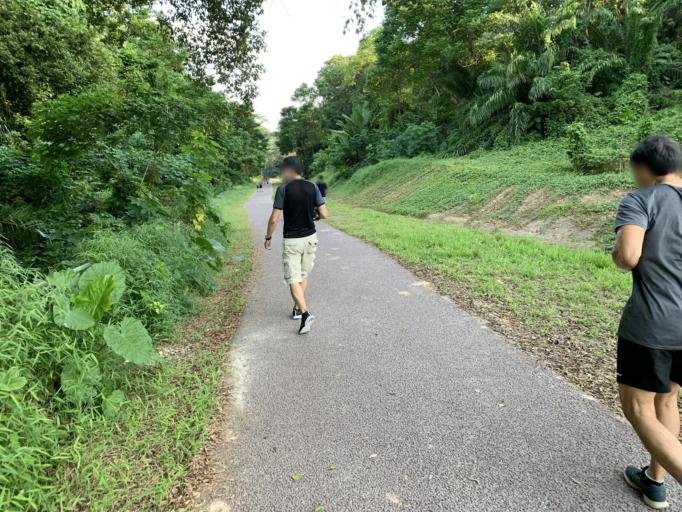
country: SG
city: Singapore
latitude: 1.3284
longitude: 103.7815
